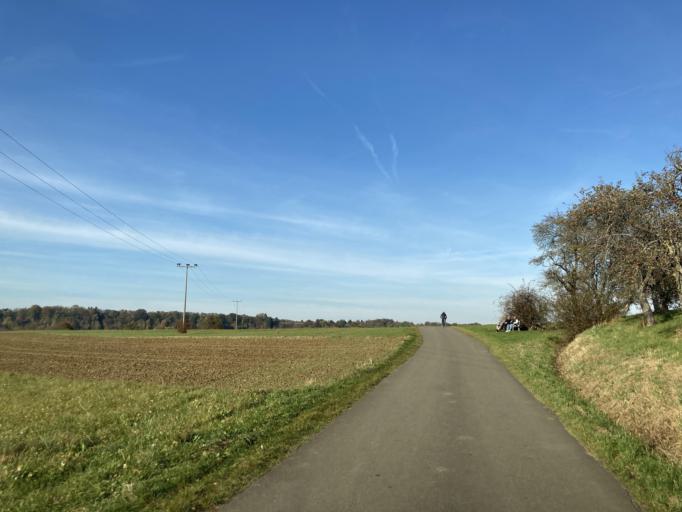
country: DE
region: Baden-Wuerttemberg
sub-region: Tuebingen Region
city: Nehren
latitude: 48.4082
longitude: 9.1004
